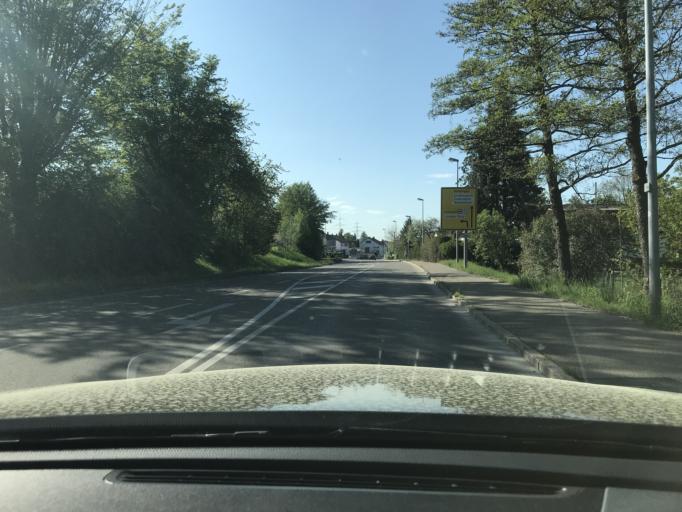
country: DE
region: Baden-Wuerttemberg
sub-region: Regierungsbezirk Stuttgart
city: Weinstadt-Endersbach
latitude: 48.7986
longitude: 9.3932
